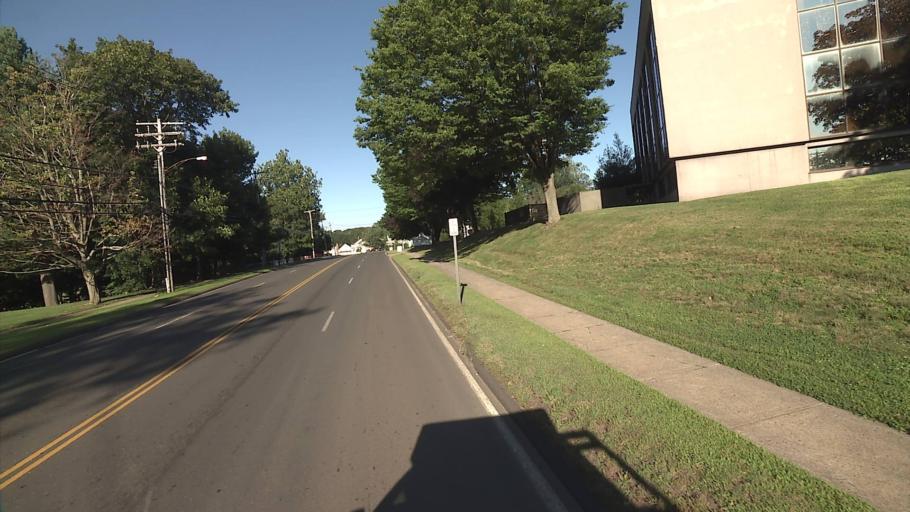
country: US
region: Connecticut
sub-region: New Haven County
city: Hamden
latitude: 41.3829
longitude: -72.9082
